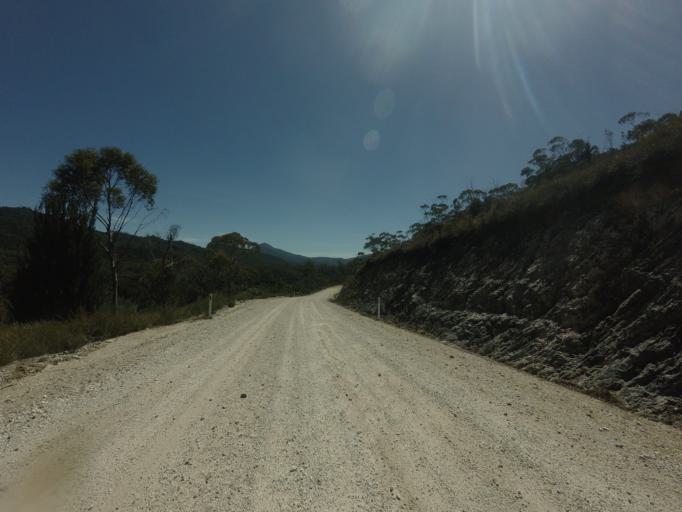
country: AU
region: Tasmania
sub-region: Huon Valley
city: Geeveston
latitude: -42.9310
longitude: 146.3416
